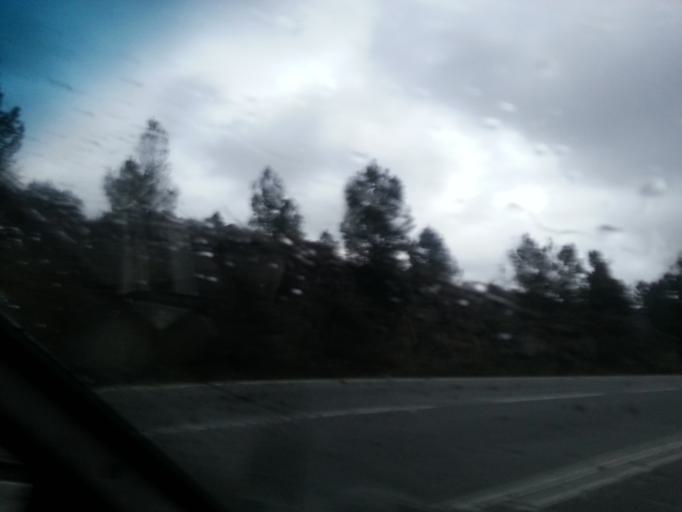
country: PT
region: Guarda
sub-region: Fornos de Algodres
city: Fornos de Algodres
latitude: 40.6035
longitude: -7.5634
